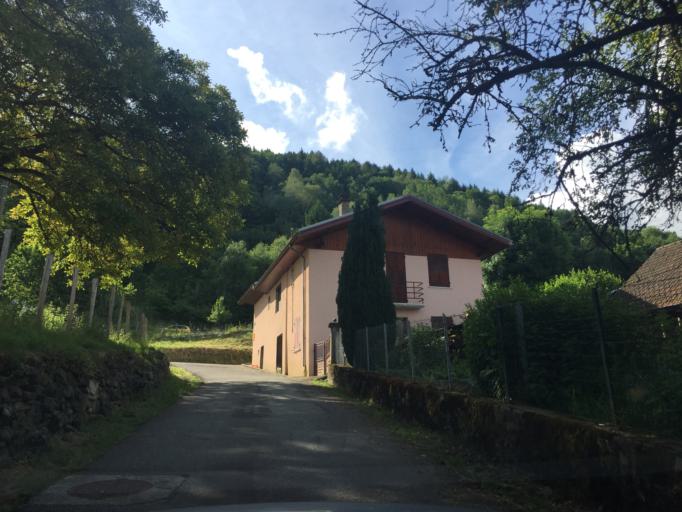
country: FR
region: Rhone-Alpes
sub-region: Departement de la Savoie
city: La Rochette
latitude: 45.4408
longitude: 6.1289
